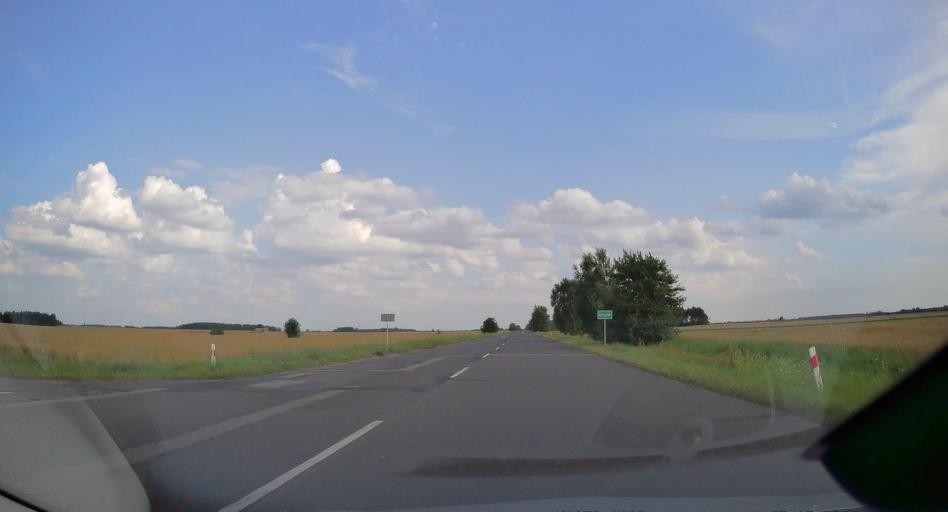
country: PL
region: Lodz Voivodeship
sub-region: Powiat tomaszowski
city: Rzeczyca
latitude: 51.6642
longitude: 20.2668
